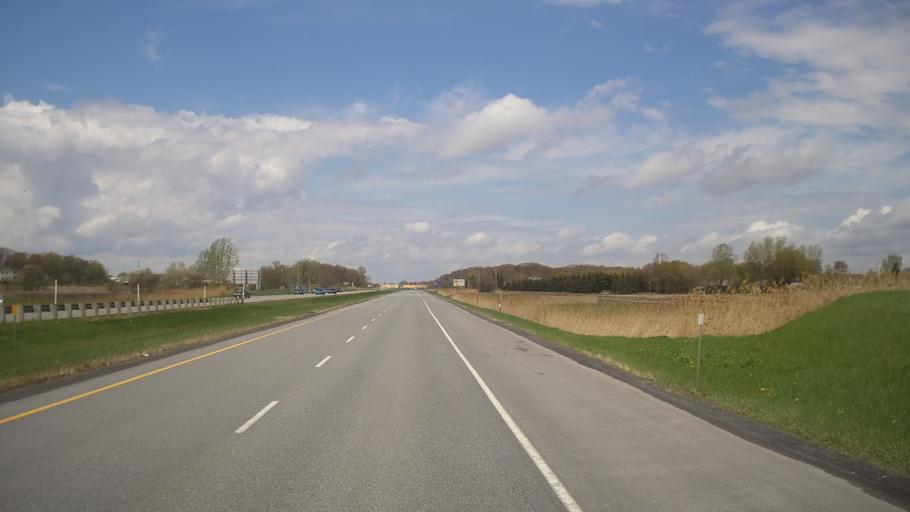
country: CA
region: Quebec
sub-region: Monteregie
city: Saint-Jean-sur-Richelieu
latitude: 45.3228
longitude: -73.2332
